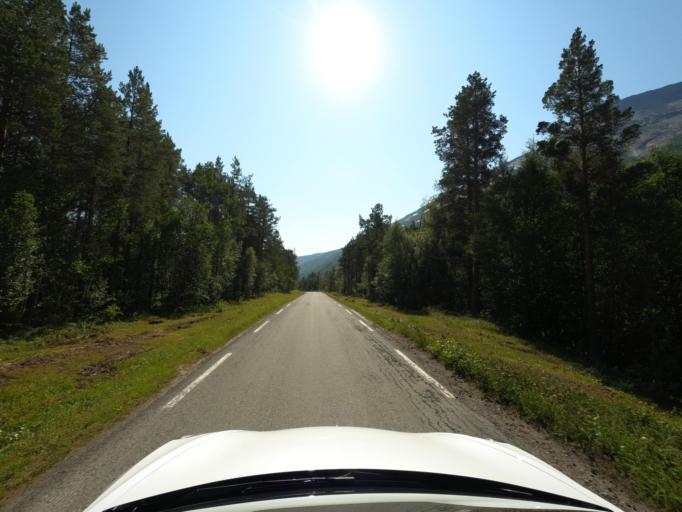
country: NO
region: Nordland
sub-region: Narvik
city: Narvik
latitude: 68.1914
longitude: 17.5535
